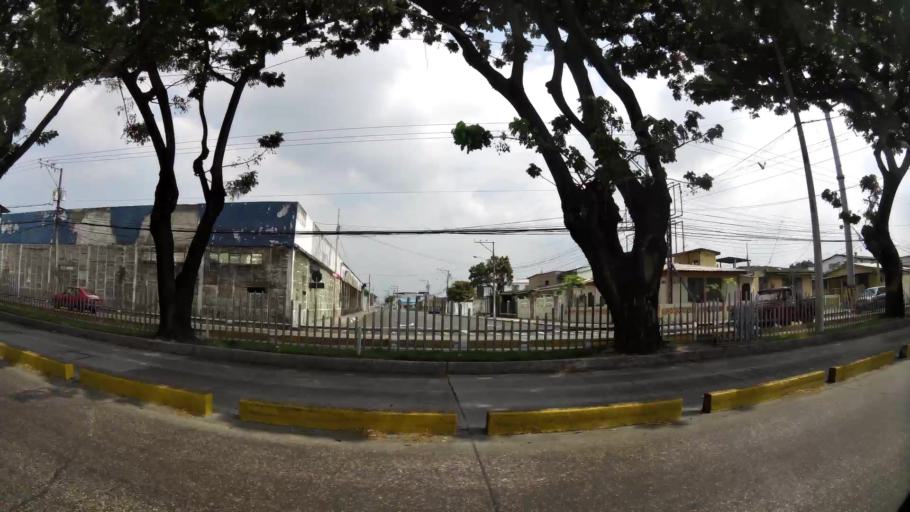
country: EC
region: Guayas
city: Guayaquil
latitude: -2.2358
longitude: -79.8908
